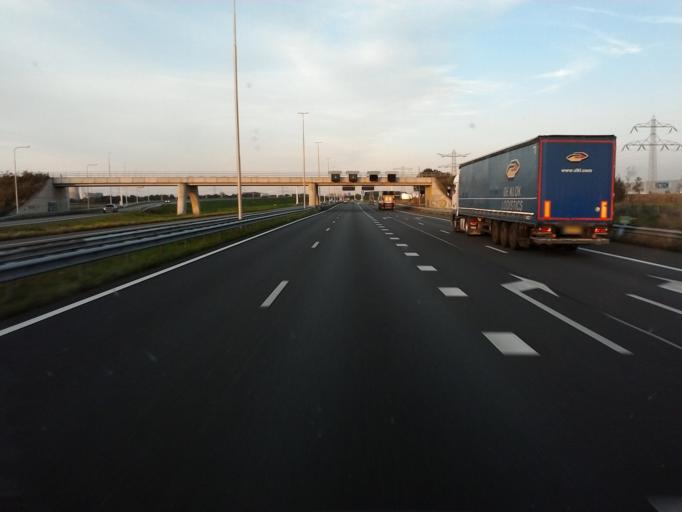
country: NL
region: Limburg
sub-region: Gemeente Maasgouw
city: Maasbracht
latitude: 51.1211
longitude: 5.8801
